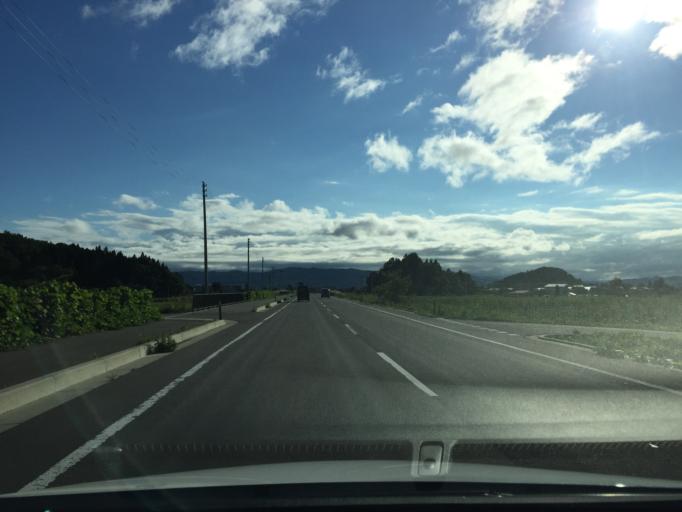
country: JP
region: Yamagata
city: Yonezawa
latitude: 37.9287
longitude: 140.1607
